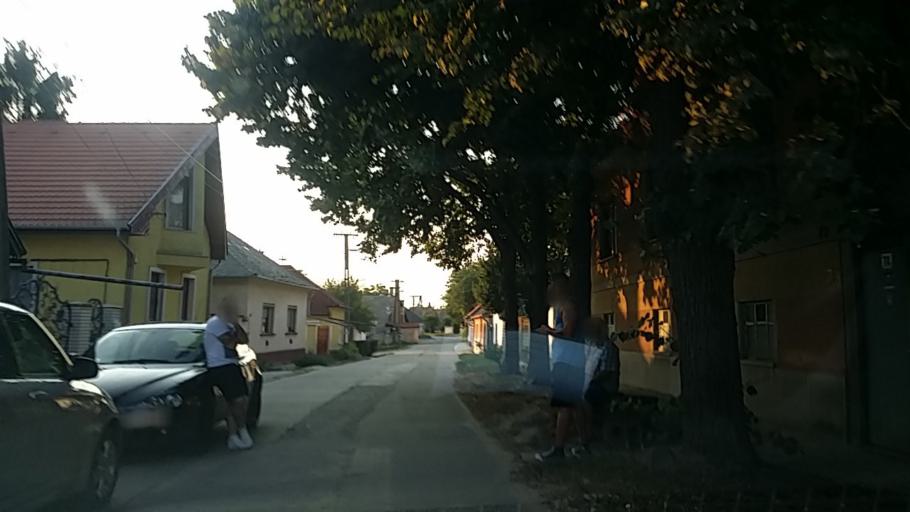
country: HU
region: Tolna
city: Dunafoldvar
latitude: 46.8132
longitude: 18.9216
